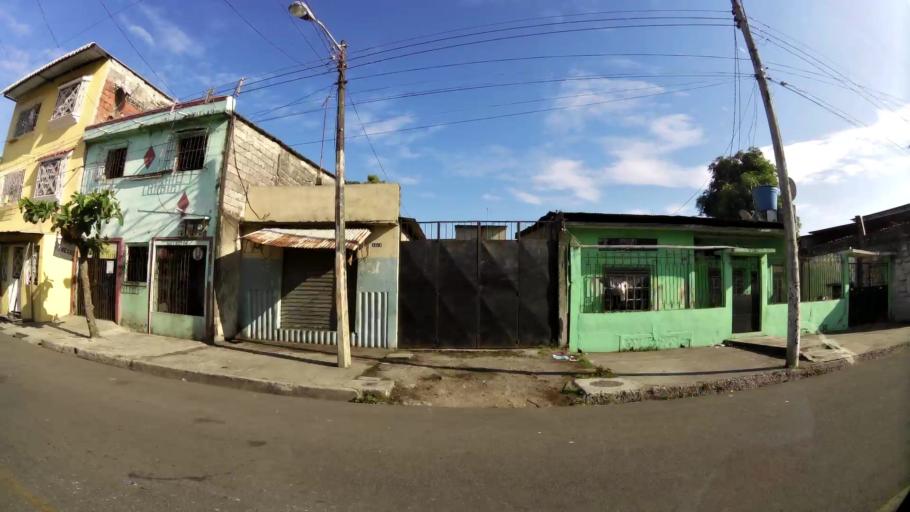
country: EC
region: Guayas
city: Guayaquil
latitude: -2.2099
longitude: -79.9254
